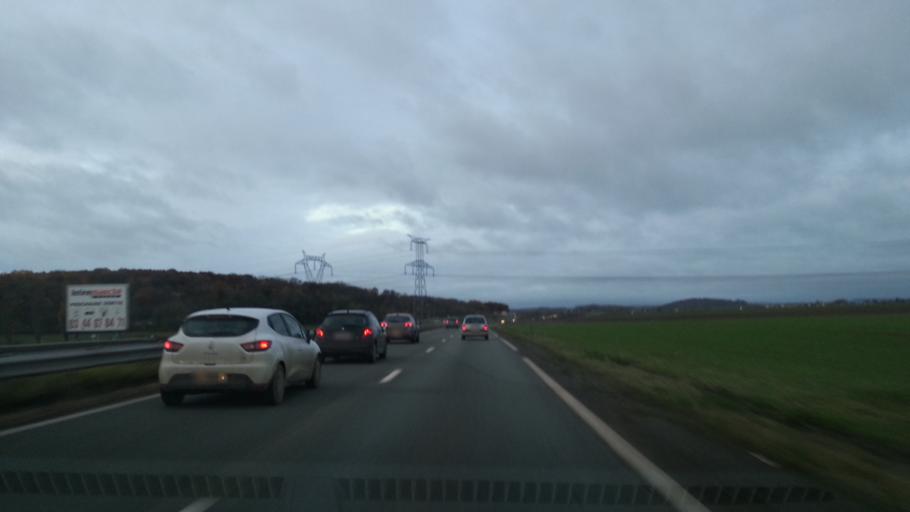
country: FR
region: Picardie
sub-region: Departement de l'Oise
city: Bresles
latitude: 49.4146
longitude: 2.2295
